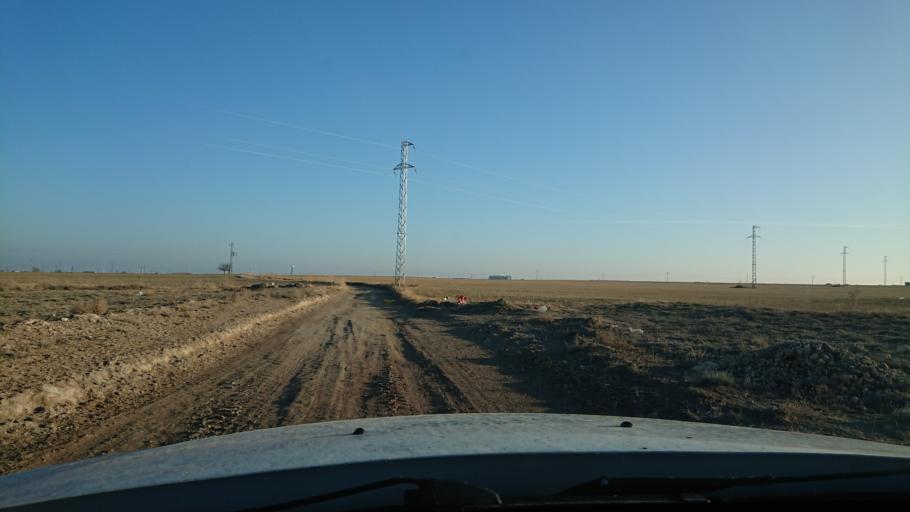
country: TR
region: Aksaray
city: Sultanhani
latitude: 38.2706
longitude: 33.5162
